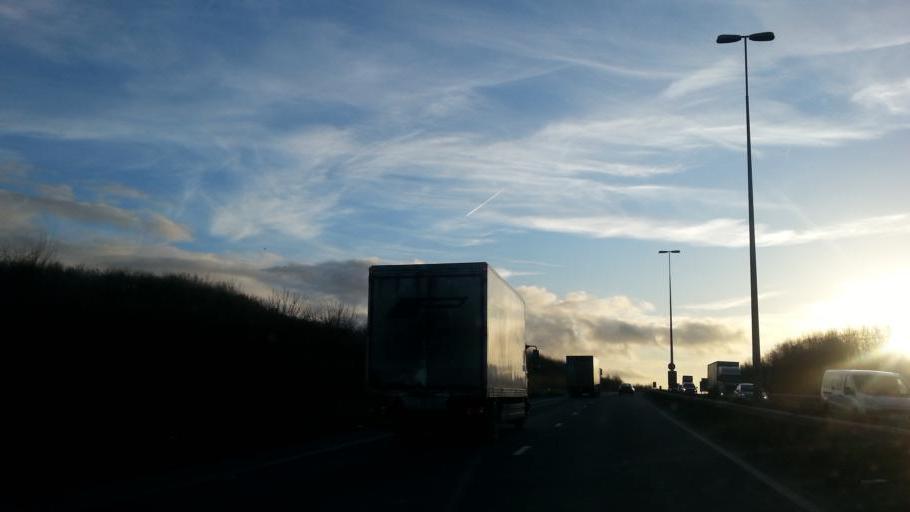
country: GB
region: England
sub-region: Northamptonshire
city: Brackley
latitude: 51.9960
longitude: -1.1611
